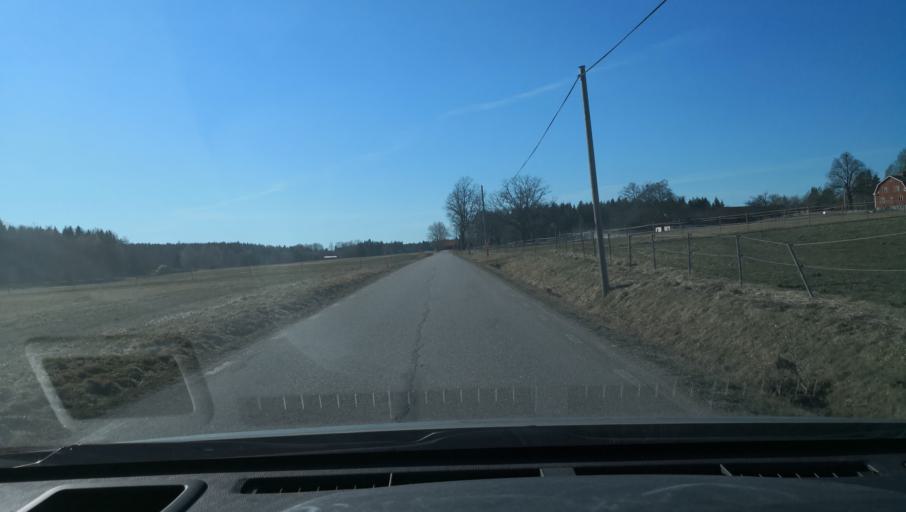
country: SE
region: Vaestmanland
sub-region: Sala Kommun
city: Sala
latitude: 60.0790
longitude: 16.4661
